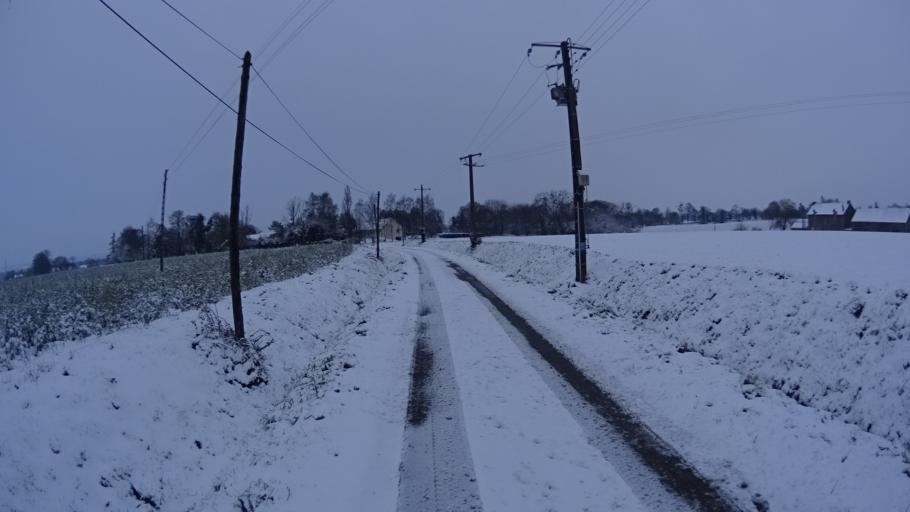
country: FR
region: Brittany
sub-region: Departement des Cotes-d'Armor
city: Evran
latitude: 48.3286
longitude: -1.9503
